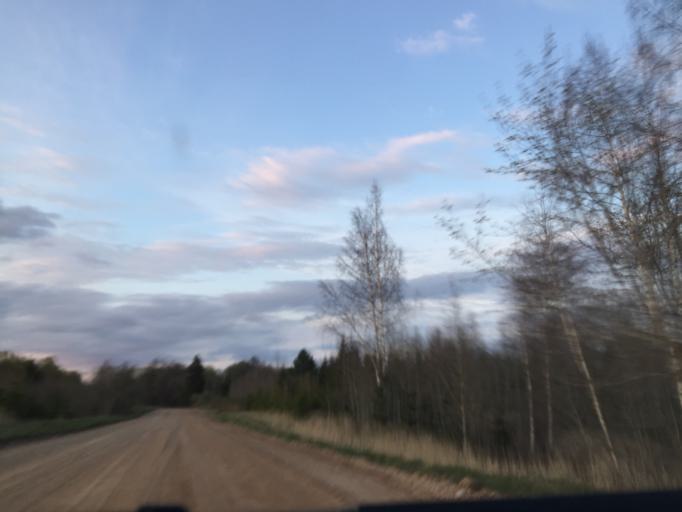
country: LV
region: Aluksnes Rajons
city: Aluksne
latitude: 57.3400
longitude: 26.9619
